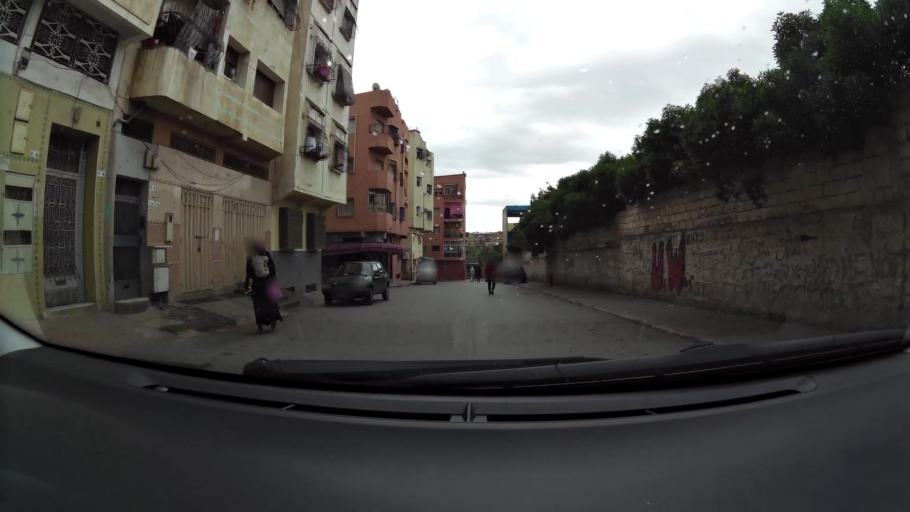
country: MA
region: Grand Casablanca
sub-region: Mediouna
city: Tit Mellil
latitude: 33.5695
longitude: -7.5360
